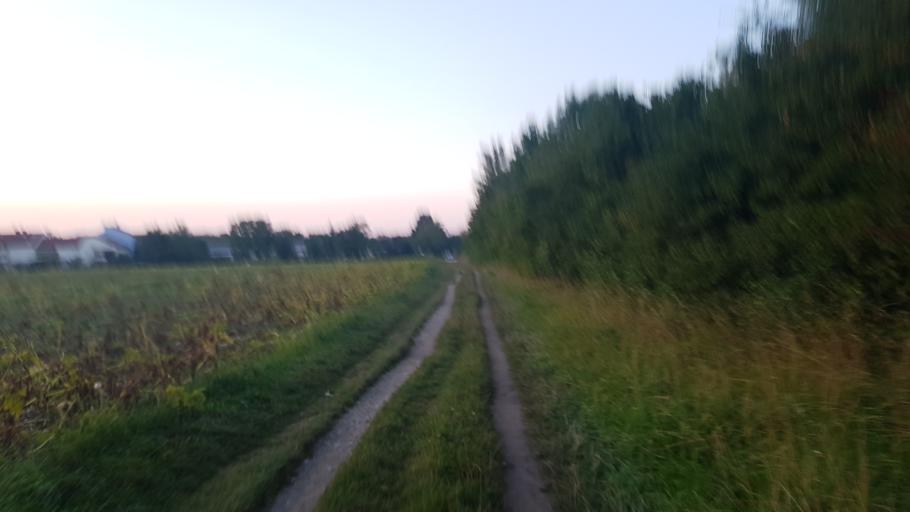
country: DE
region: Bavaria
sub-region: Upper Bavaria
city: Pasing
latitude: 48.1318
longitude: 11.4613
